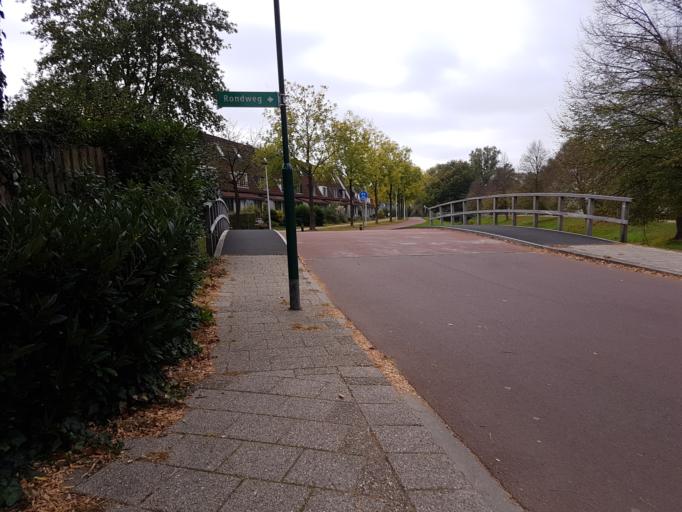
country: NL
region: Utrecht
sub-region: Gemeente Houten
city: Houten
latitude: 52.0397
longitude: 5.1735
